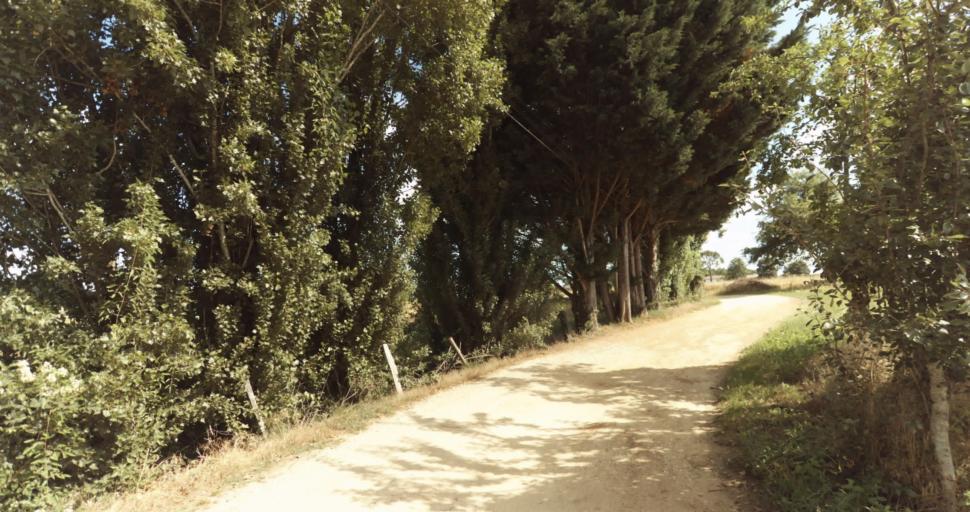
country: FR
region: Aquitaine
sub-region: Departement de la Gironde
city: Bazas
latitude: 44.4384
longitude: -0.1946
